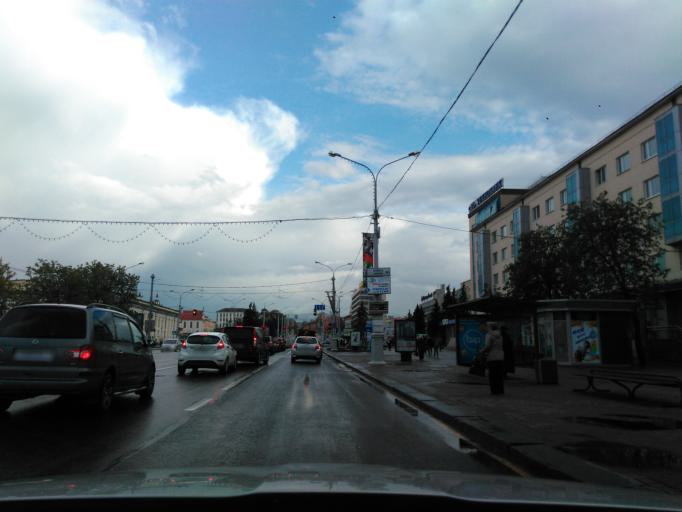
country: BY
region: Minsk
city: Minsk
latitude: 53.9081
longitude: 27.5505
